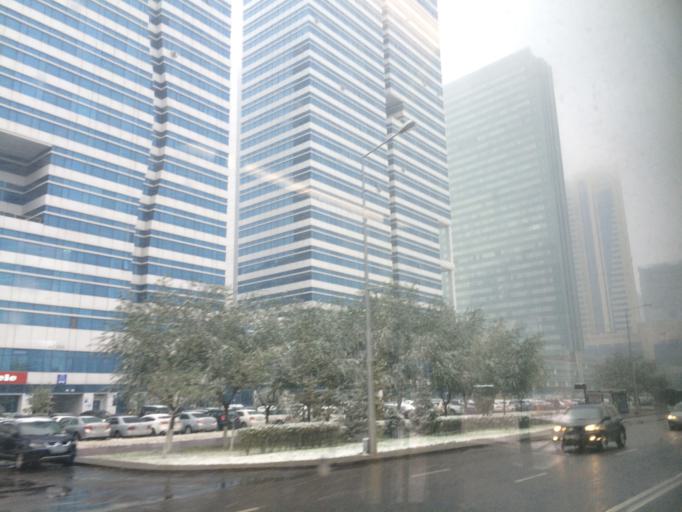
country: KZ
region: Astana Qalasy
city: Astana
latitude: 51.1311
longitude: 71.4279
